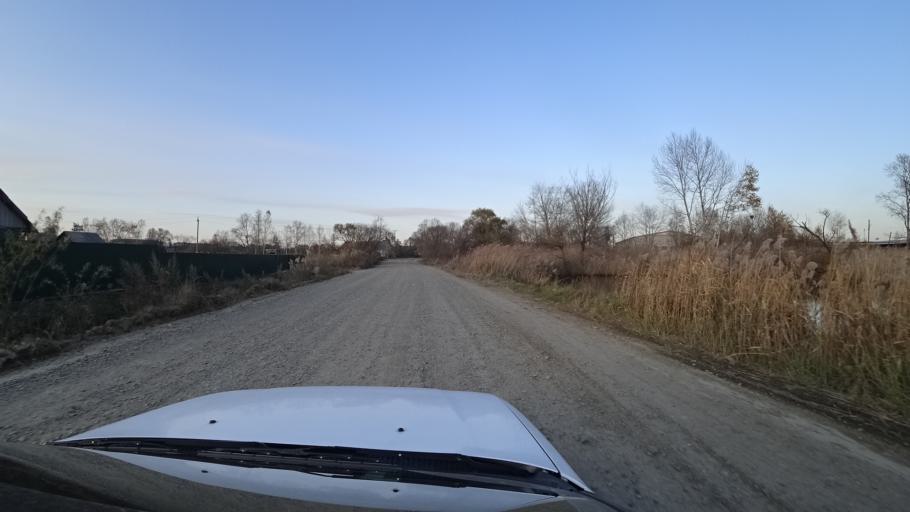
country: RU
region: Primorskiy
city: Dal'nerechensk
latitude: 45.9394
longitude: 133.8210
